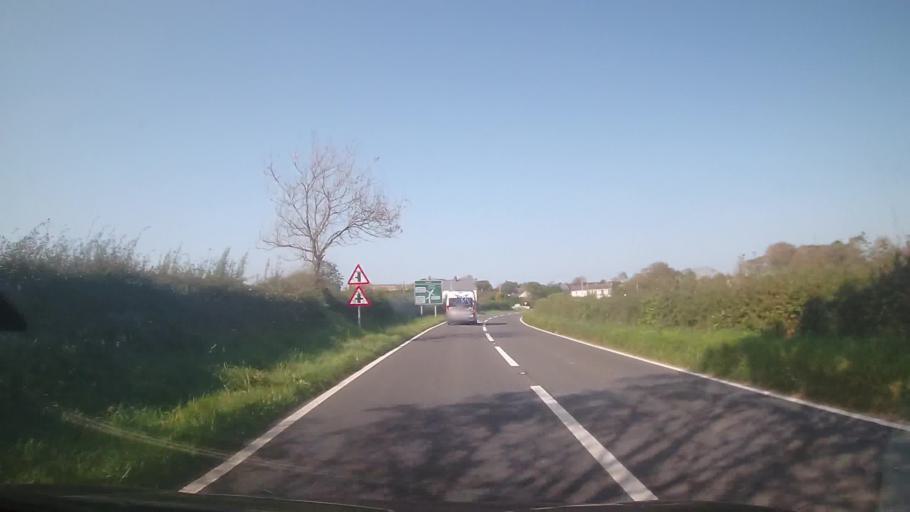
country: GB
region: Wales
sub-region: County of Ceredigion
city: Cardigan
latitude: 52.0522
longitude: -4.6914
